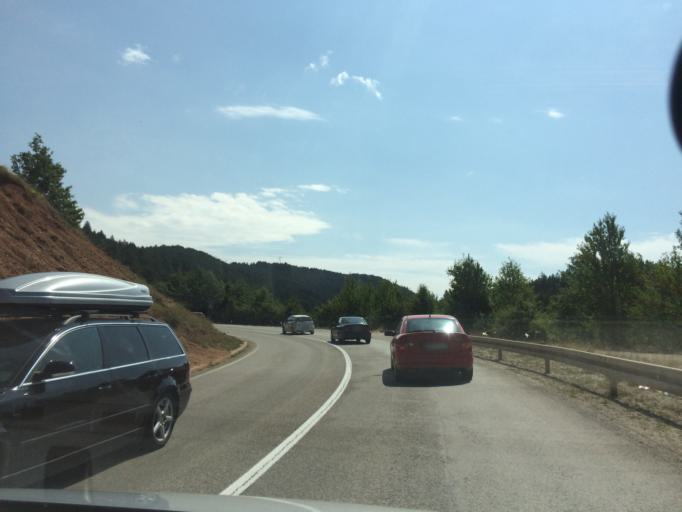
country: RS
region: Central Serbia
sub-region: Zlatiborski Okrug
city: Nova Varos
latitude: 43.5737
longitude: 19.7500
